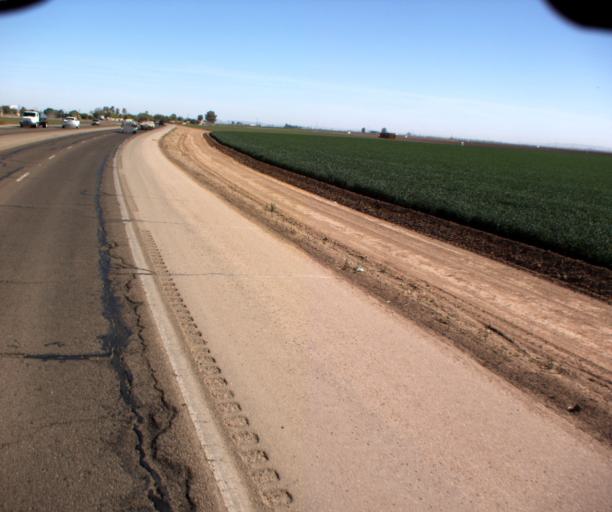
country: US
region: Arizona
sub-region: Yuma County
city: San Luis
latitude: 32.5471
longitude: -114.7865
